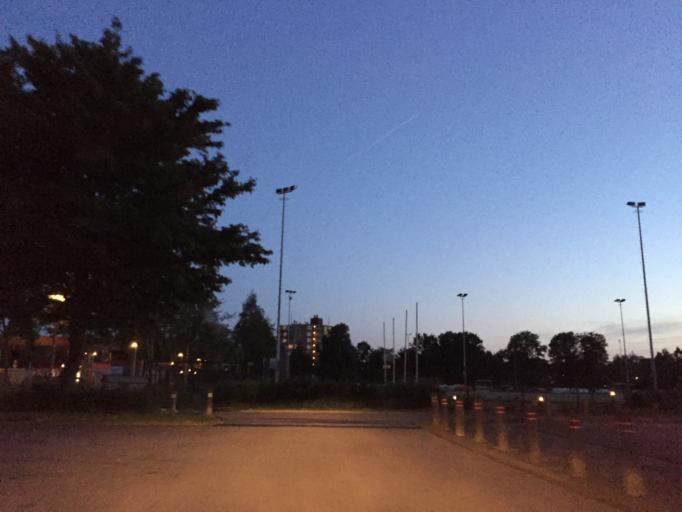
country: NL
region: South Holland
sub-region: Gemeente Waddinxveen
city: Groenswaard
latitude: 52.0431
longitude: 4.6419
